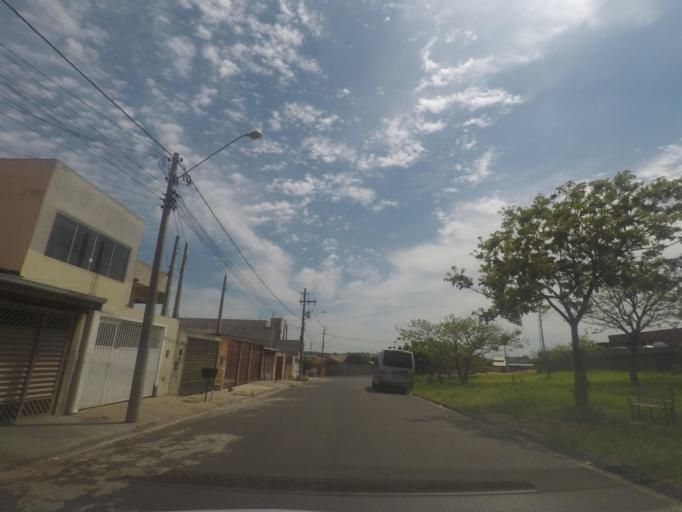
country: BR
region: Sao Paulo
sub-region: Sumare
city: Sumare
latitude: -22.8030
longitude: -47.2630
